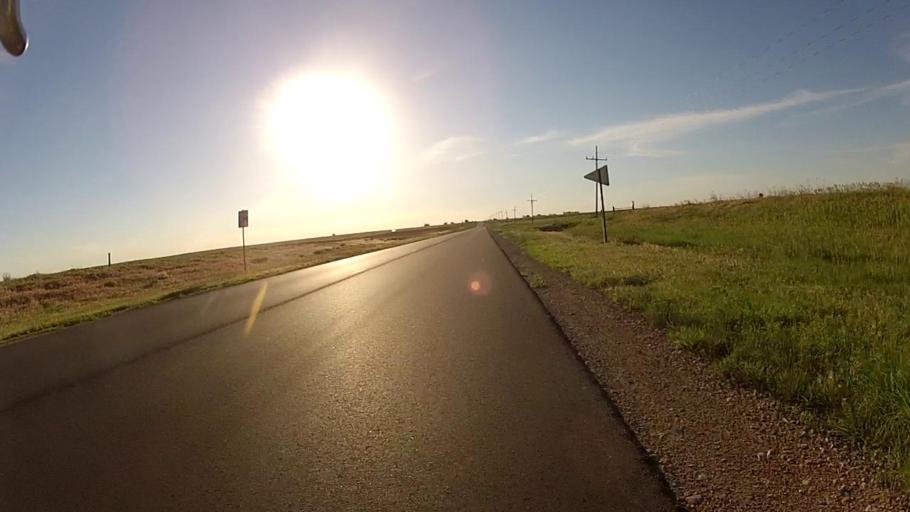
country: US
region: Kansas
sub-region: Comanche County
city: Coldwater
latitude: 37.2814
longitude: -99.1887
